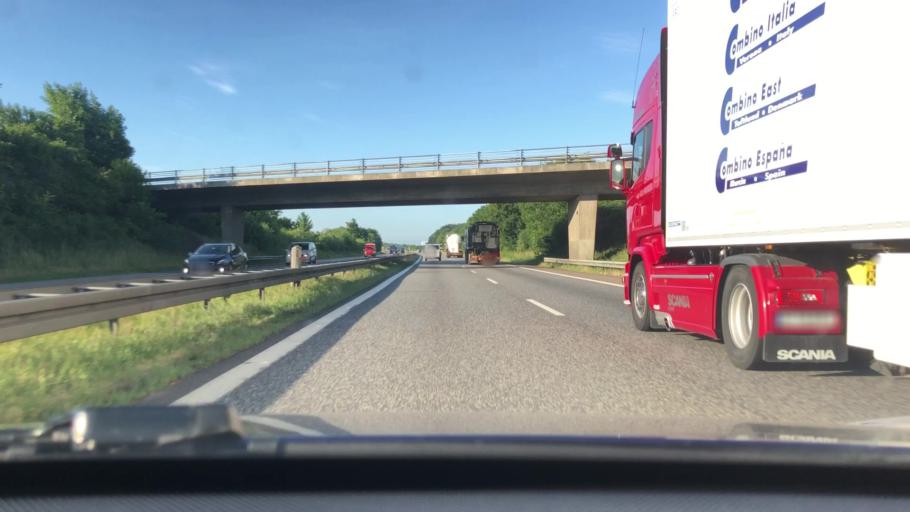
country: DK
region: South Denmark
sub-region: Kolding Kommune
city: Christiansfeld
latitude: 55.3095
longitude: 9.4317
